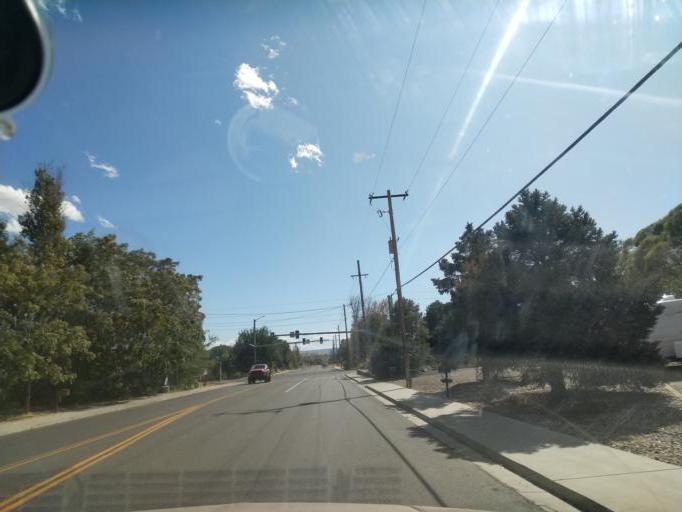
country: US
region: Colorado
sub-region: Mesa County
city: Clifton
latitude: 39.0927
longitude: -108.4409
